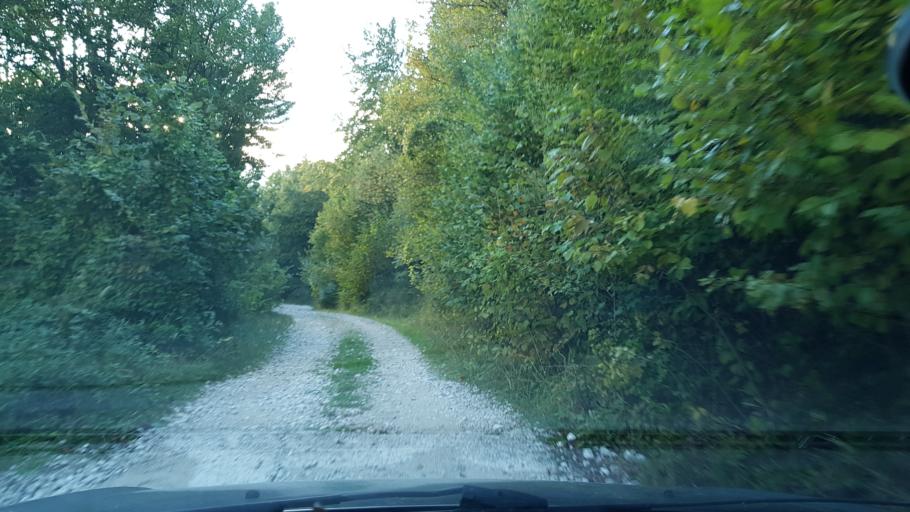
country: SI
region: Kobarid
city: Kobarid
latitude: 46.2760
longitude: 13.6221
